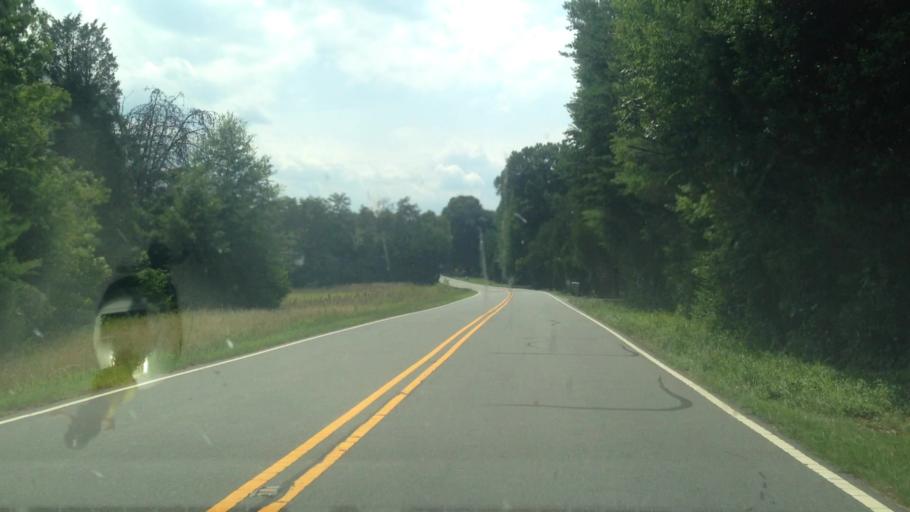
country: US
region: North Carolina
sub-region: Stokes County
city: Walnut Cove
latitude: 36.3719
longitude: -80.0730
